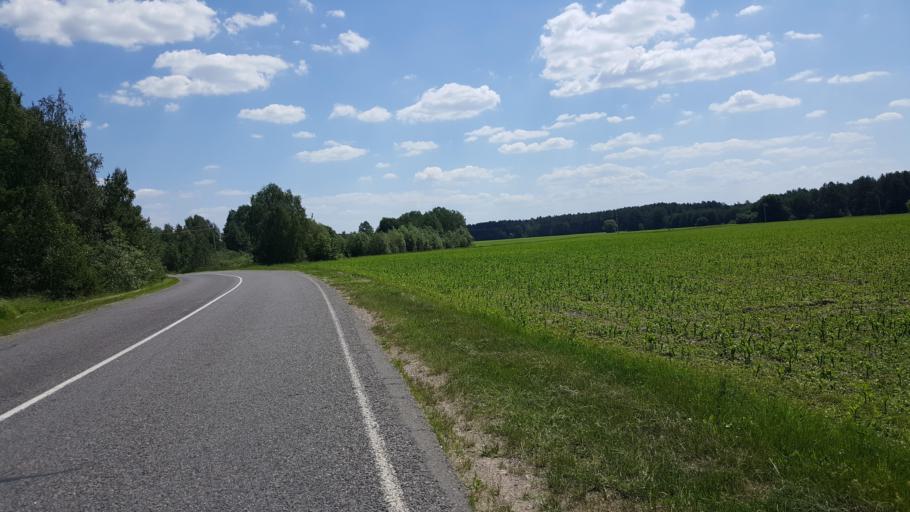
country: BY
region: Brest
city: Zhabinka
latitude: 52.1983
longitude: 24.1208
